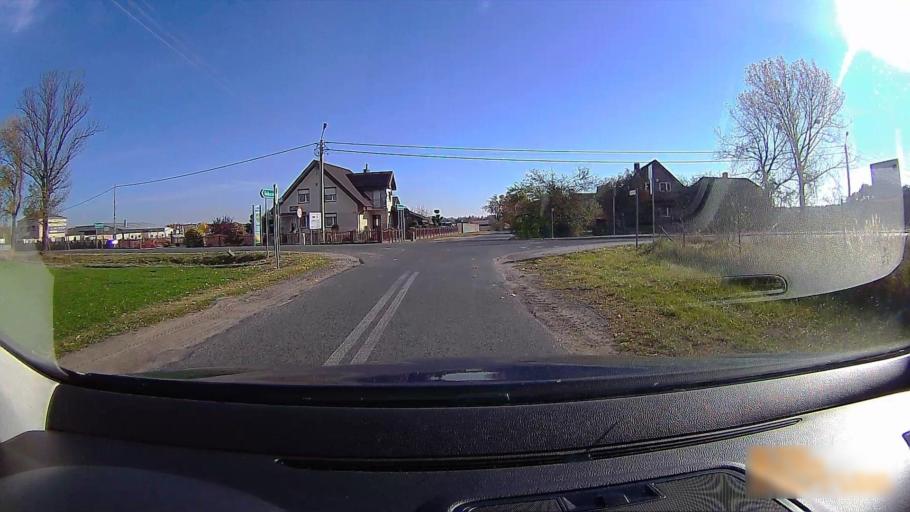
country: PL
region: Greater Poland Voivodeship
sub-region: Powiat ostrzeszowski
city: Doruchow
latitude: 51.3917
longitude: 18.0542
